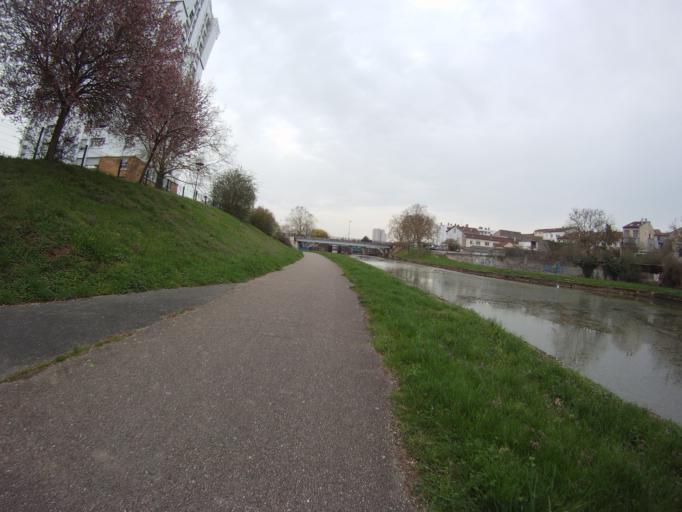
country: FR
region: Lorraine
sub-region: Departement de Meurthe-et-Moselle
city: Jarville-la-Malgrange
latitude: 48.6732
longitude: 6.2052
